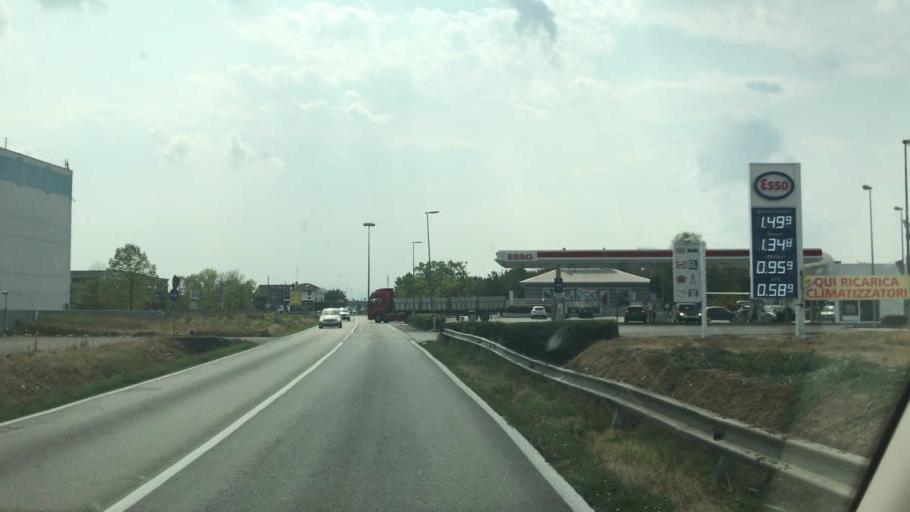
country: IT
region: Emilia-Romagna
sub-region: Provincia di Parma
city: Baganzola
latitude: 44.8501
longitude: 10.3416
